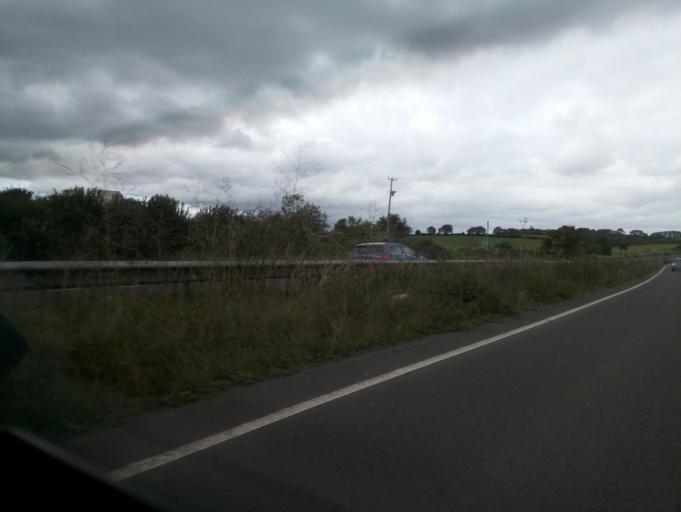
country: GB
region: England
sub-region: Devon
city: Marldon
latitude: 50.4653
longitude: -3.5848
